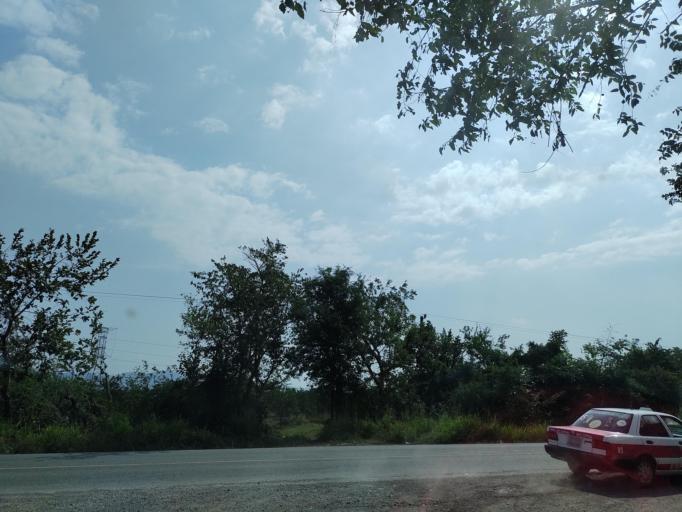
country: MX
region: Puebla
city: Espinal
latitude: 20.2808
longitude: -97.3311
